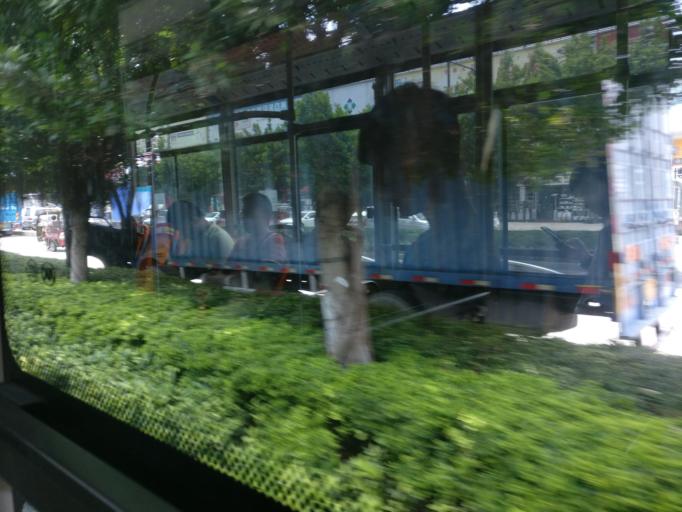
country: CN
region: Guangdong
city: Dashi
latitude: 23.0370
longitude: 113.3313
